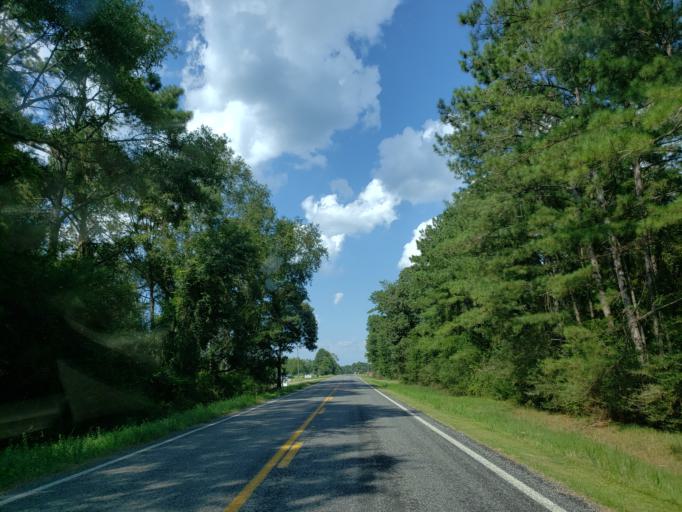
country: US
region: Mississippi
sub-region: Covington County
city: Collins
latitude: 31.6084
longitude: -89.4344
